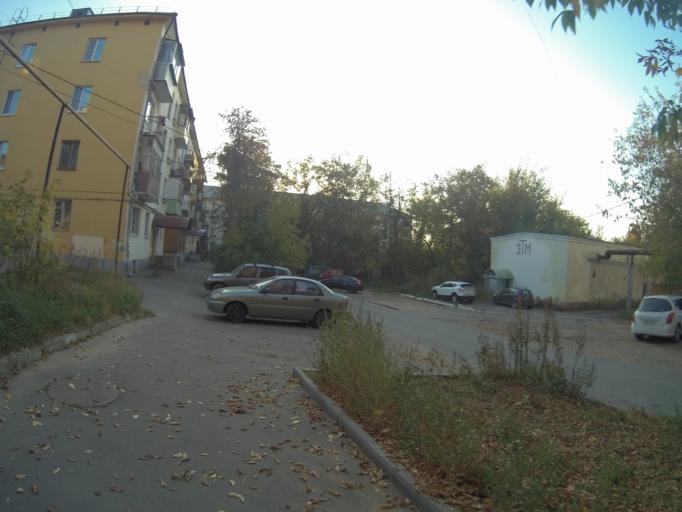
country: RU
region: Vladimir
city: Vladimir
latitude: 56.1169
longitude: 40.3453
